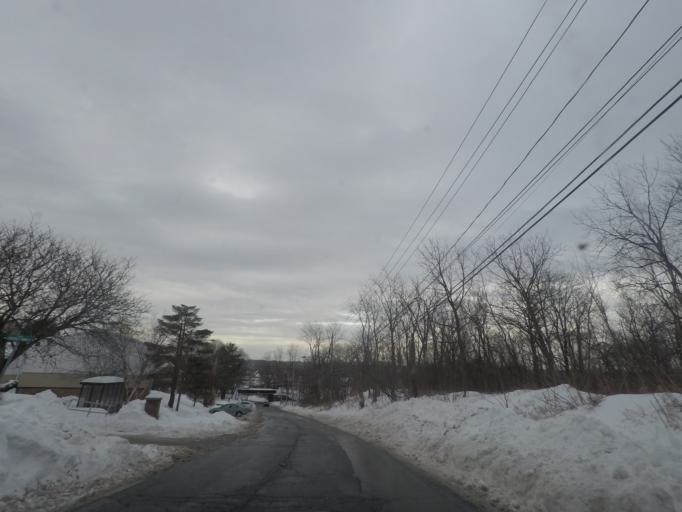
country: US
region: New York
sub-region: Rensselaer County
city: Rensselaer
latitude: 42.6336
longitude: -73.7403
